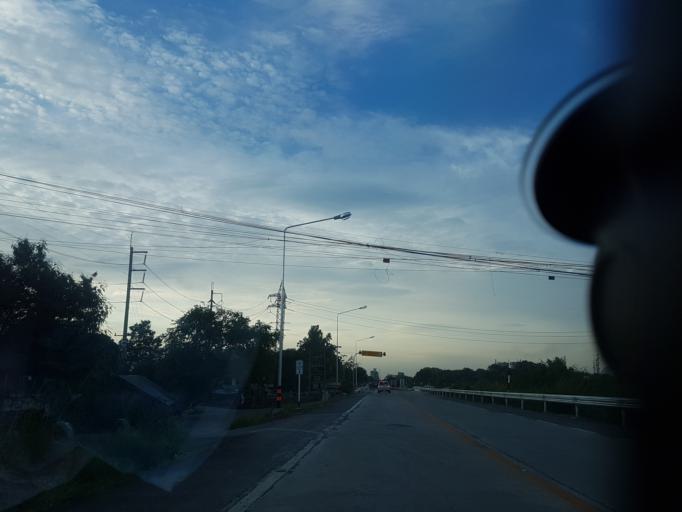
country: TH
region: Phra Nakhon Si Ayutthaya
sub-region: Amphoe Tha Ruea
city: Tha Ruea
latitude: 14.5527
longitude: 100.7623
